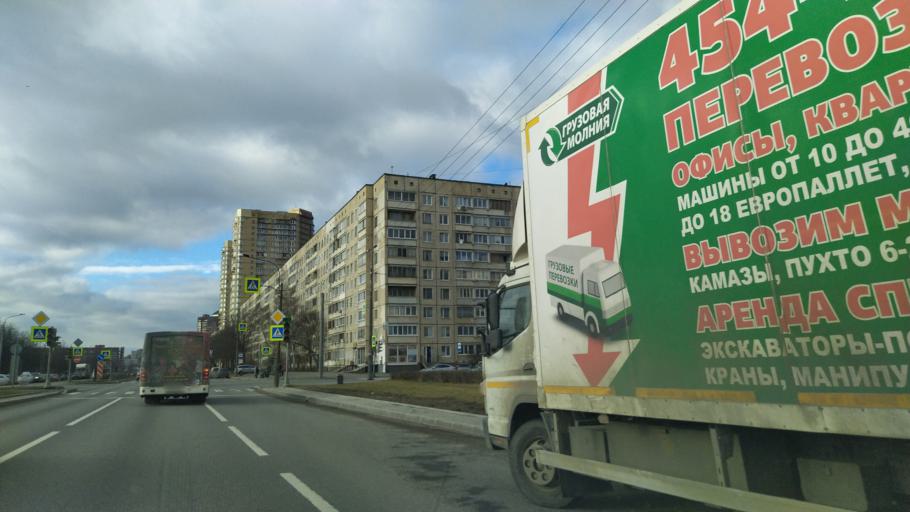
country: RU
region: Leningrad
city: Akademicheskoe
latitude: 60.0333
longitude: 30.3804
